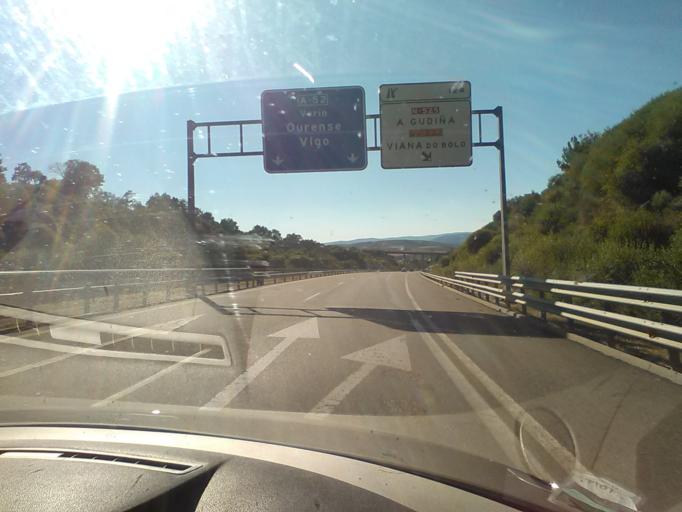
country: ES
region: Castille and Leon
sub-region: Provincia de Zamora
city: Pias
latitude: 42.0562
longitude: -7.1102
